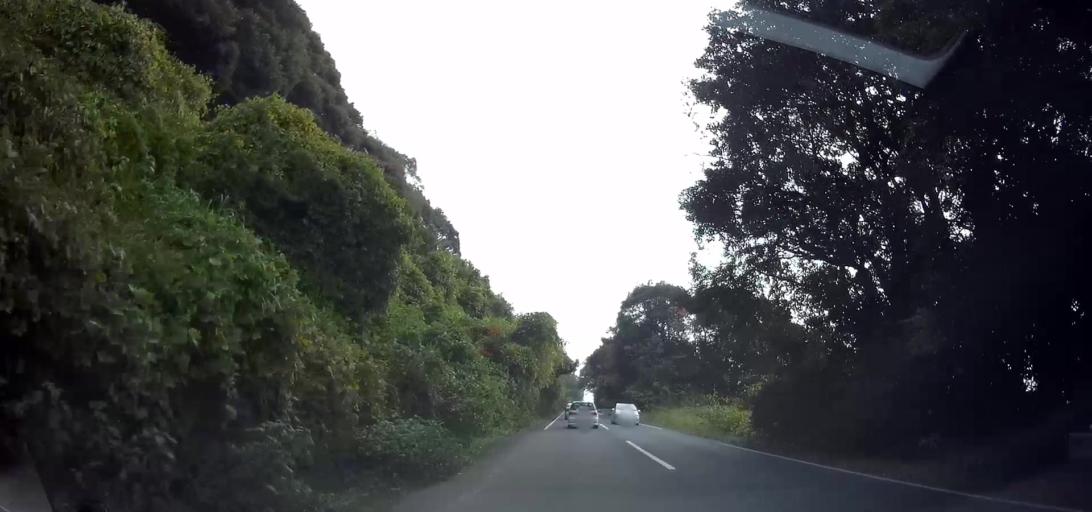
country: JP
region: Nagasaki
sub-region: Isahaya-shi
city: Isahaya
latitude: 32.7945
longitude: 130.1057
